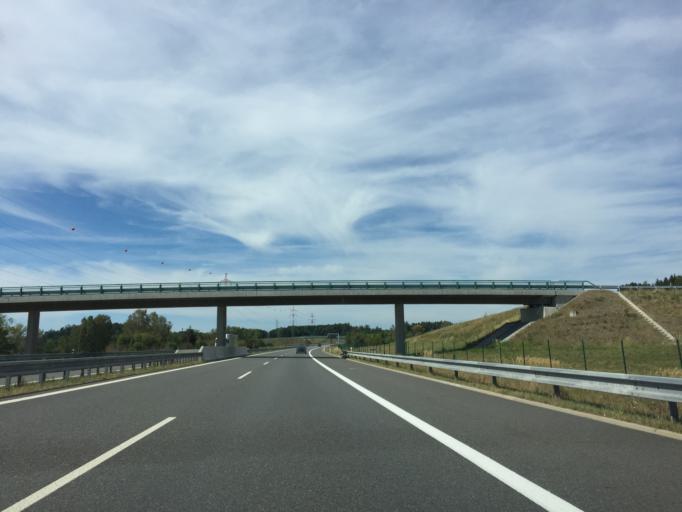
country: CZ
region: Jihocesky
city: Plana nad Luznici
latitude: 49.3454
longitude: 14.7310
